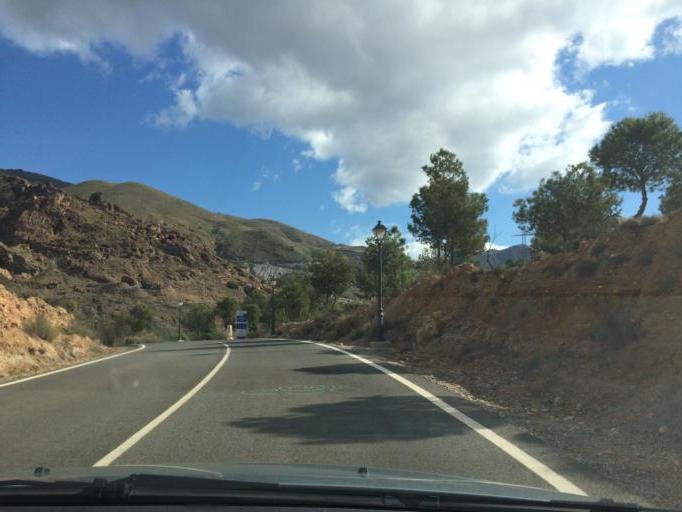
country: ES
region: Andalusia
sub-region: Provincia de Almeria
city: Pechina
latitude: 36.9599
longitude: -2.4013
